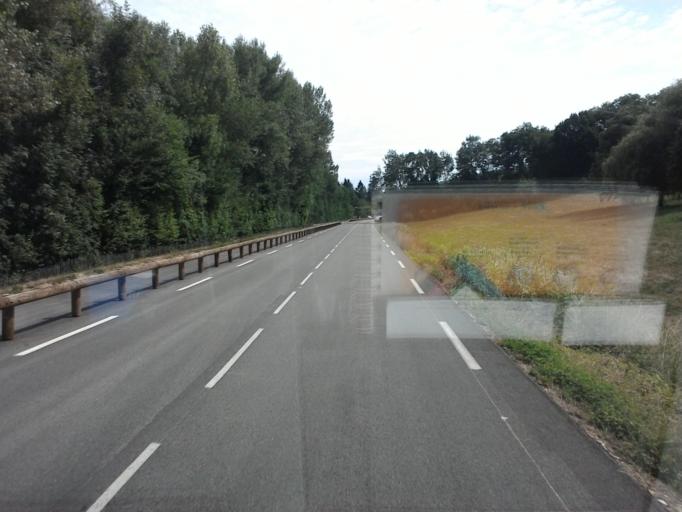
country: FR
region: Rhone-Alpes
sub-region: Departement de l'Isere
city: Bilieu
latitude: 45.4642
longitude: 5.5521
